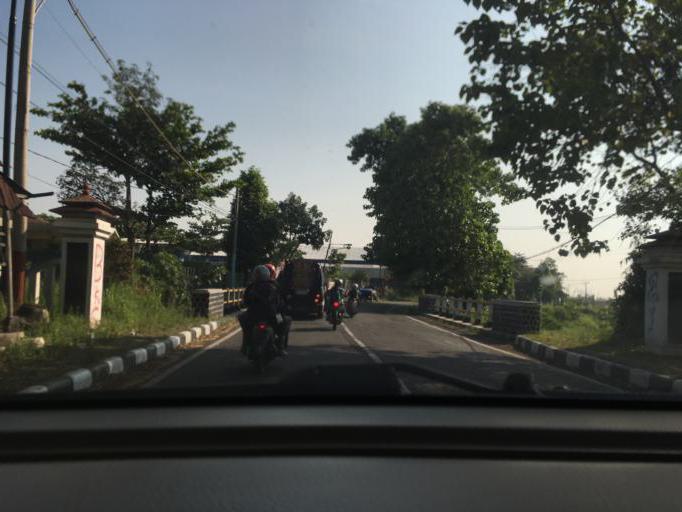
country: ID
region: West Java
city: Kuningan
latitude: -6.8995
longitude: 108.4910
